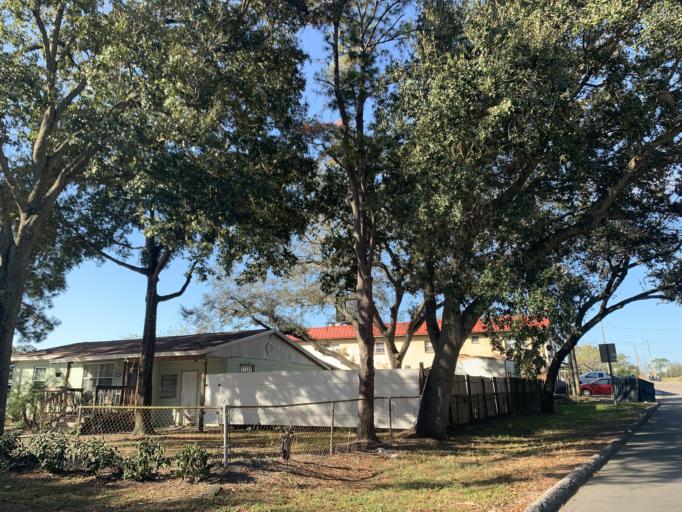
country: US
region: Florida
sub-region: Hillsborough County
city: Temple Terrace
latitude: 28.0316
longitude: -82.4154
